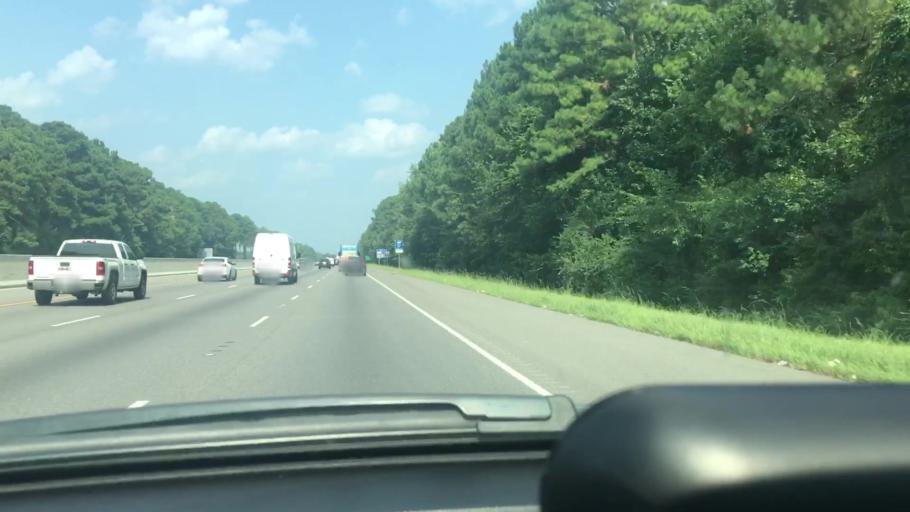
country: US
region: Louisiana
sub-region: Livingston Parish
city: Denham Springs
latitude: 30.4584
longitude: -90.9425
